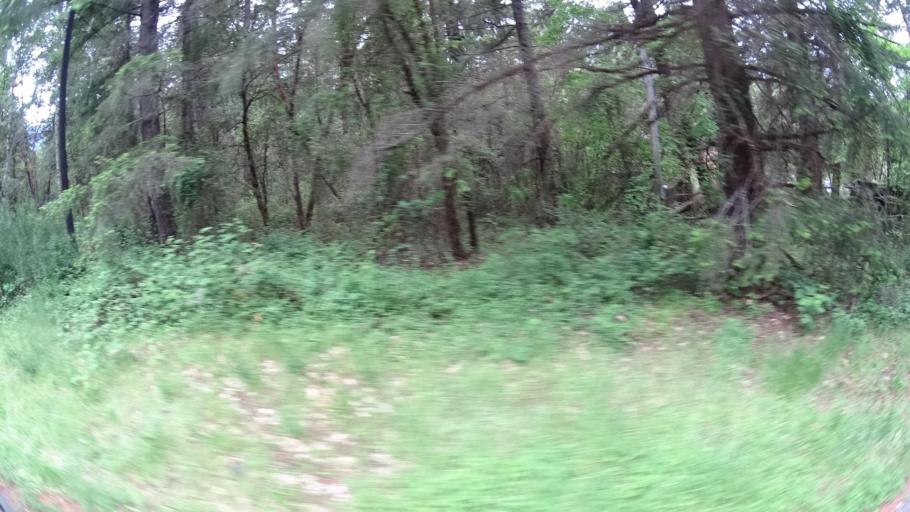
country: US
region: California
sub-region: Humboldt County
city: Willow Creek
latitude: 41.0425
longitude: -123.6597
